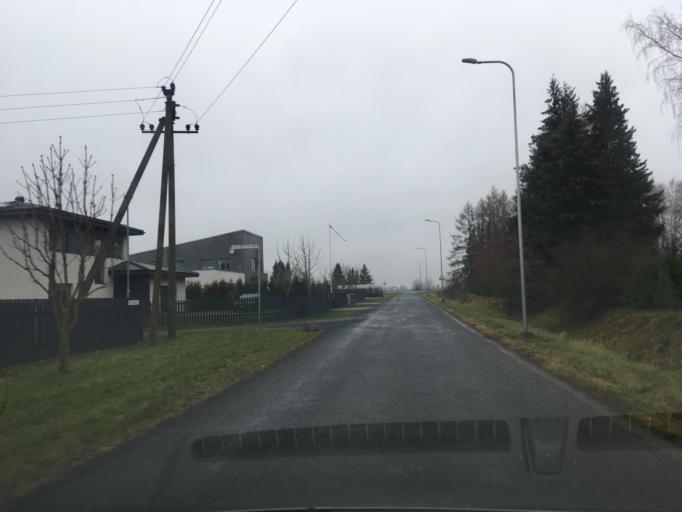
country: EE
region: Tartu
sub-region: Tartu linn
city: Tartu
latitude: 58.3546
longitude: 26.8712
